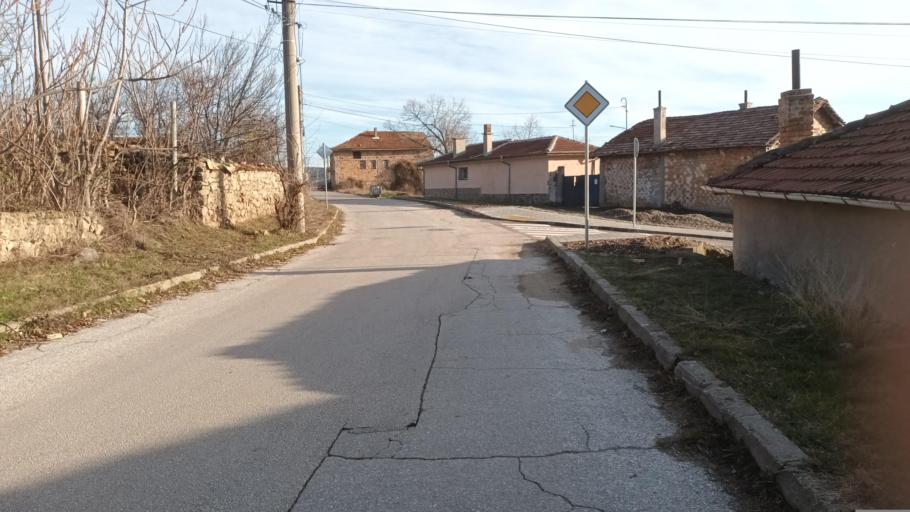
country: BG
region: Plovdiv
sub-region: Obshtina Khisarya
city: Khisarya
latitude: 42.5224
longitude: 24.7220
